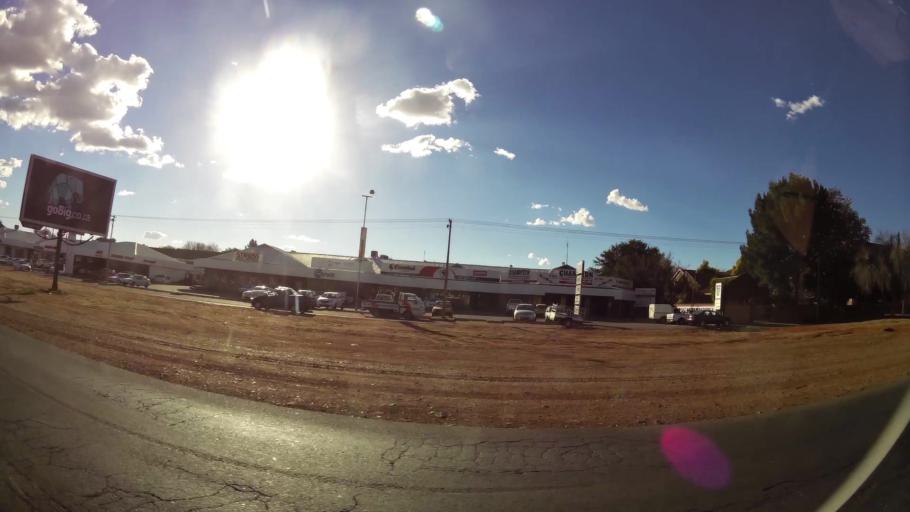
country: ZA
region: North-West
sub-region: Dr Kenneth Kaunda District Municipality
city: Klerksdorp
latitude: -26.8539
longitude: 26.6825
